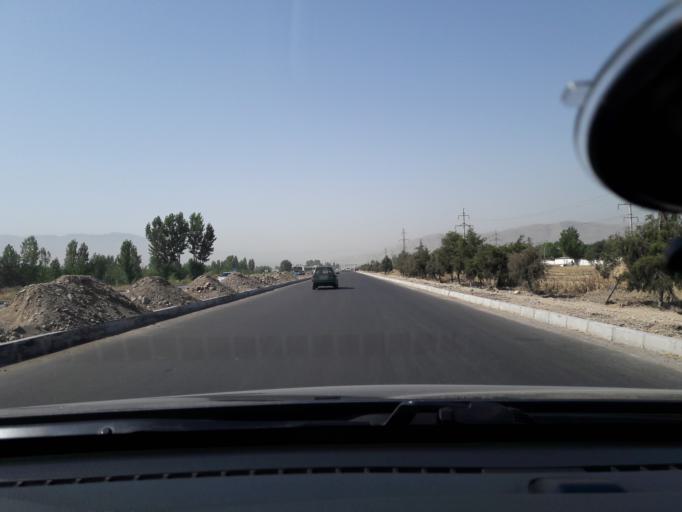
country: TJ
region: Dushanbe
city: Dushanbe
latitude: 38.4892
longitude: 68.7507
